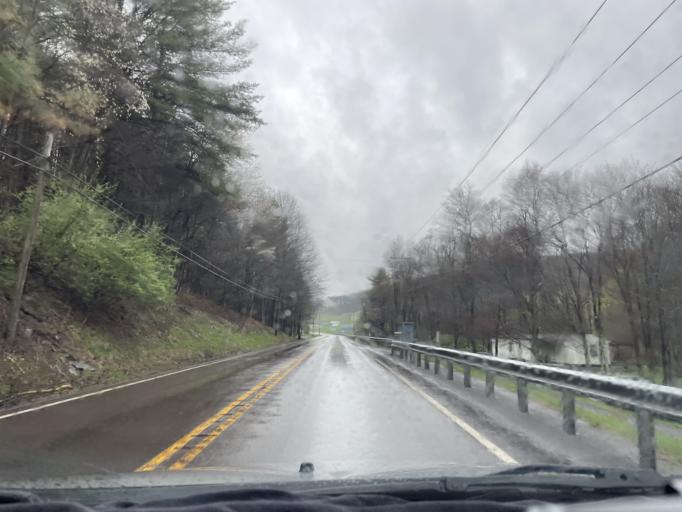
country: US
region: Maryland
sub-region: Garrett County
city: Mountain Lake Park
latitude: 39.4540
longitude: -79.2561
